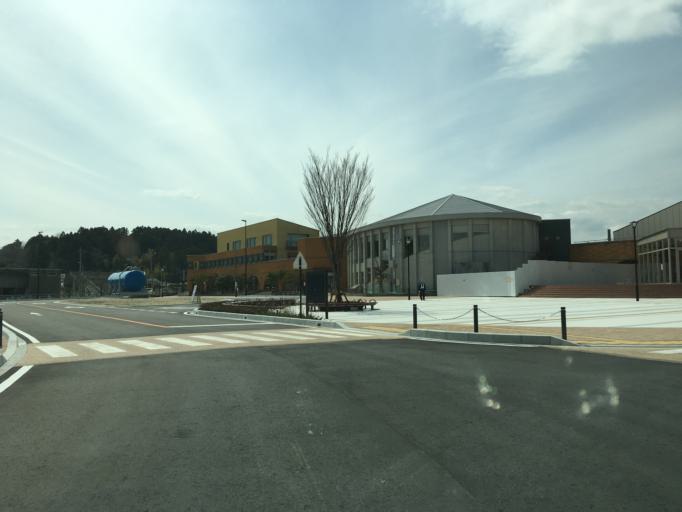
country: JP
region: Fukushima
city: Namie
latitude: 37.4537
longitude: 141.0066
